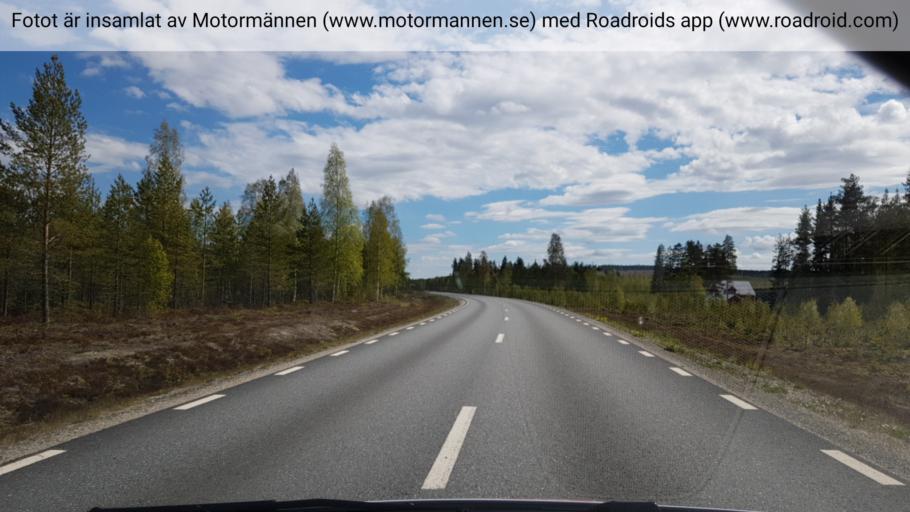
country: SE
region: Vaesterbotten
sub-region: Bjurholms Kommun
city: Bjurholm
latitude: 64.2965
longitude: 19.1789
